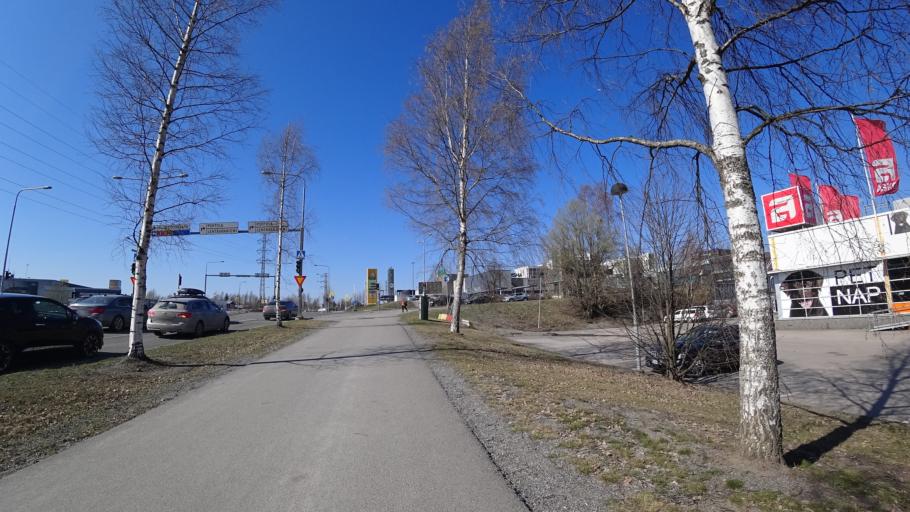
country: FI
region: Pirkanmaa
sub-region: Tampere
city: Pirkkala
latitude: 61.5179
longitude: 23.6681
